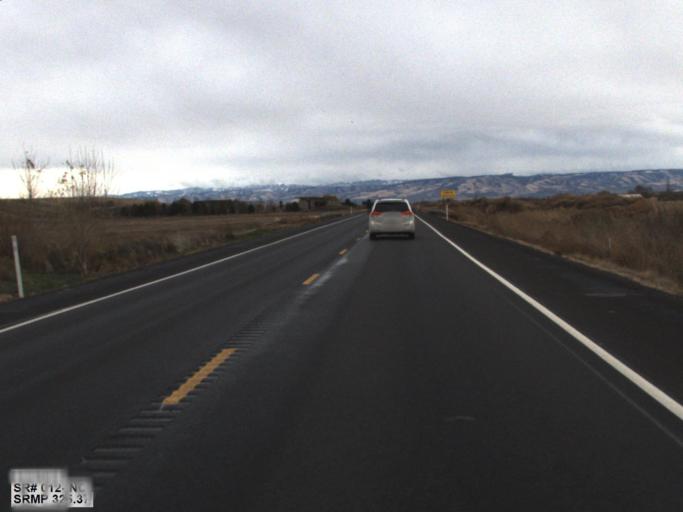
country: US
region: Washington
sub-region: Walla Walla County
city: Garrett
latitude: 46.0541
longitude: -118.5652
